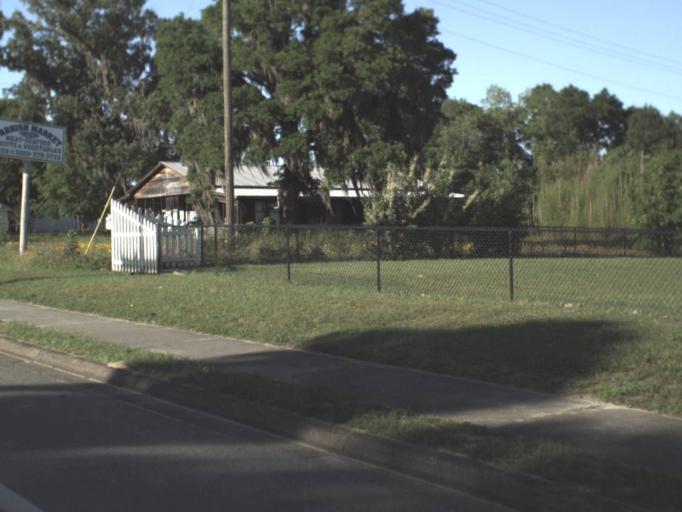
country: US
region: Florida
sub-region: Liberty County
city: Bristol
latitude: 30.3832
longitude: -84.7983
